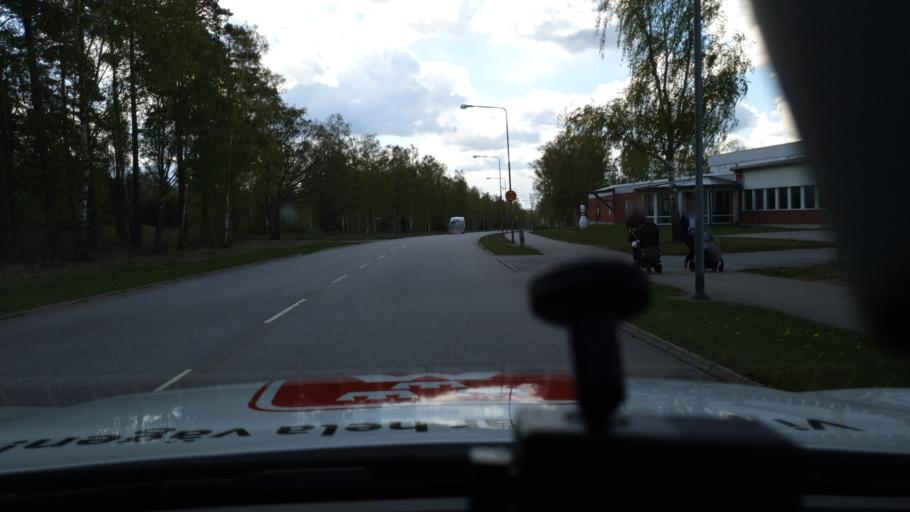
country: SE
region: Kalmar
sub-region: Vimmerby Kommun
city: Vimmerby
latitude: 57.6712
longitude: 15.8734
